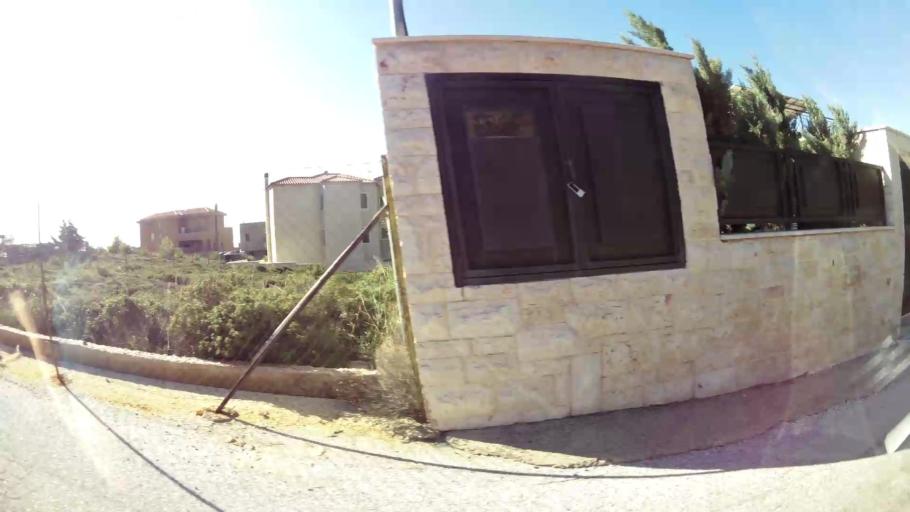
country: GR
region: Attica
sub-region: Nomarchia Anatolikis Attikis
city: Dioni
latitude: 38.0388
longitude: 23.9248
